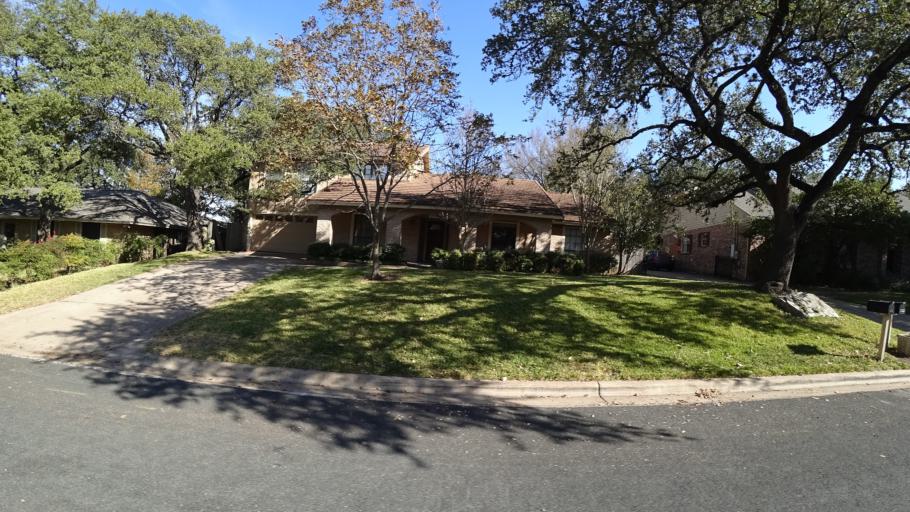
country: US
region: Texas
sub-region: Williamson County
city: Jollyville
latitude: 30.3832
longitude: -97.7602
